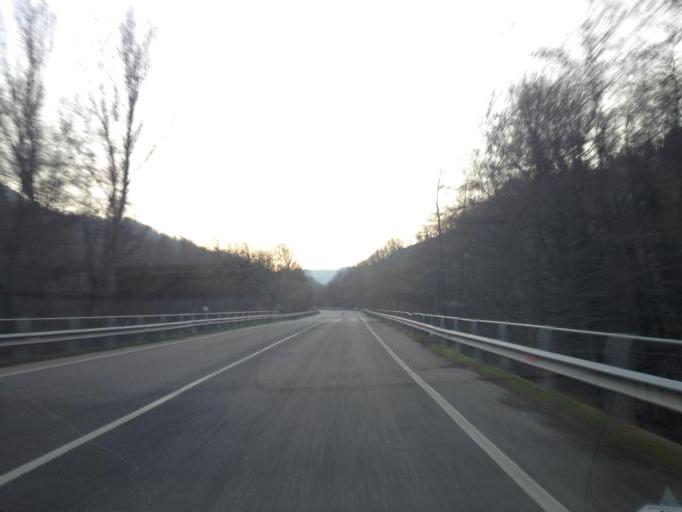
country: IT
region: The Marches
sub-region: Provincia di Ascoli Piceno
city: Arquata del Tronto
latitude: 42.7589
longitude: 13.2842
